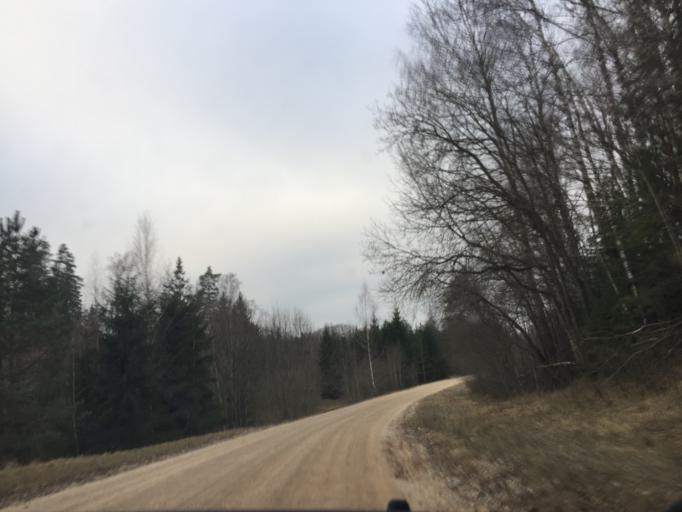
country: LV
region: Ligatne
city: Ligatne
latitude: 57.2089
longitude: 25.1366
